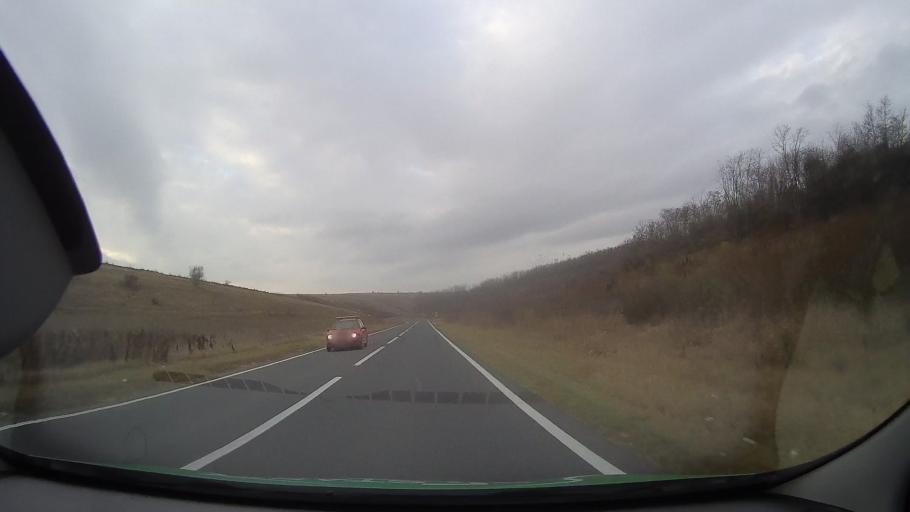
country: RO
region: Constanta
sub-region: Comuna Deleni
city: Deleni
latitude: 44.1011
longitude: 28.0282
